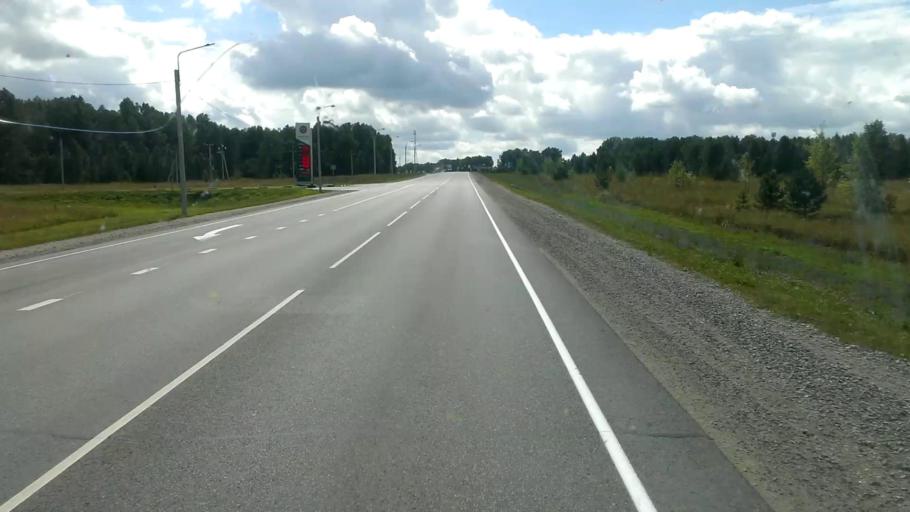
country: RU
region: Altai Krai
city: Troitskoye
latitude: 52.9749
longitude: 84.7470
